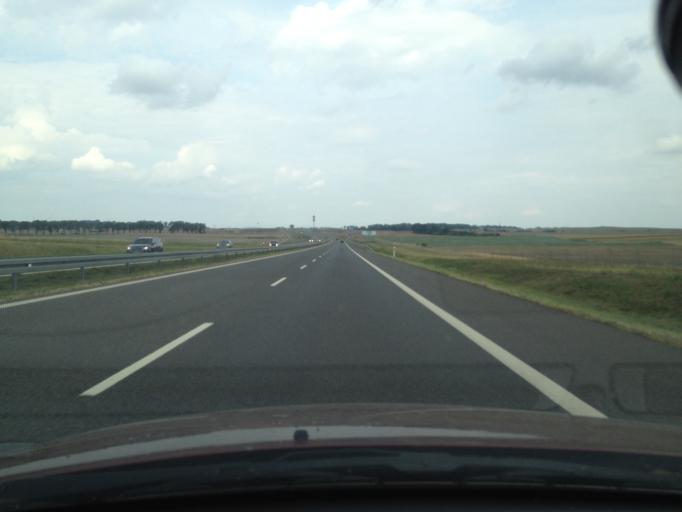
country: PL
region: West Pomeranian Voivodeship
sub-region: Powiat pyrzycki
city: Kozielice
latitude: 53.0372
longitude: 14.8650
